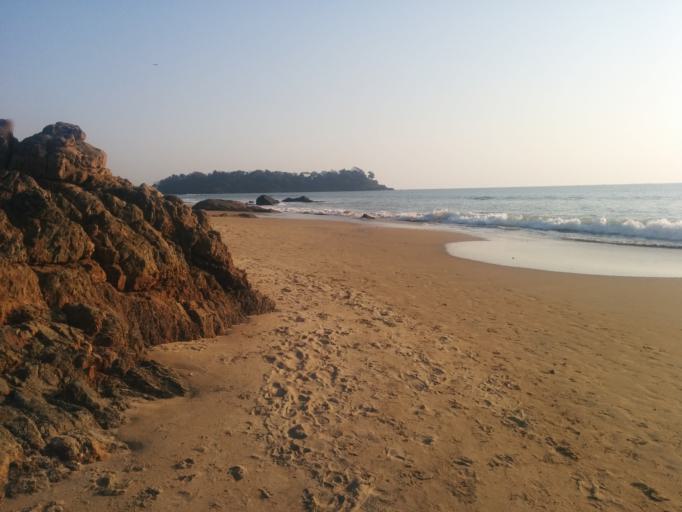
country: IN
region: Karnataka
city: Canacona
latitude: 14.9941
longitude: 74.0348
